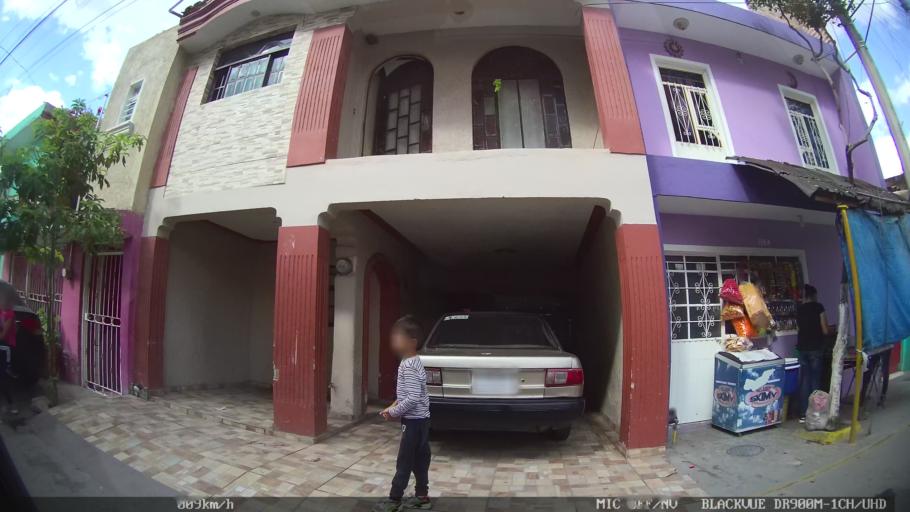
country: MX
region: Jalisco
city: Tlaquepaque
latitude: 20.6631
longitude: -103.2634
